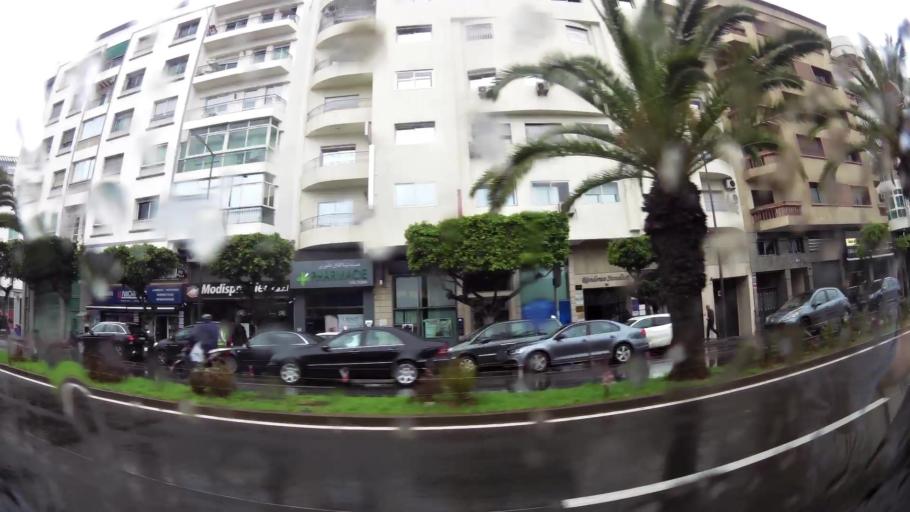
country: MA
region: Grand Casablanca
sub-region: Casablanca
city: Casablanca
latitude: 33.5751
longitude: -7.6345
